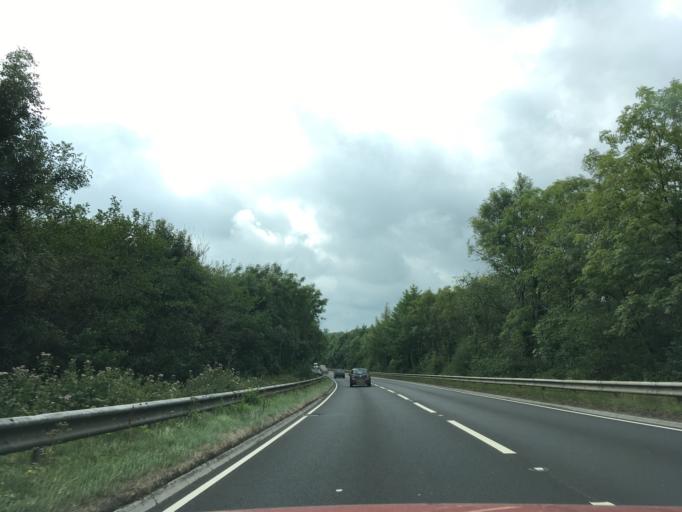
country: GB
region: Wales
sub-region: Carmarthenshire
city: Llanddowror
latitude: 51.8263
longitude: -4.5566
